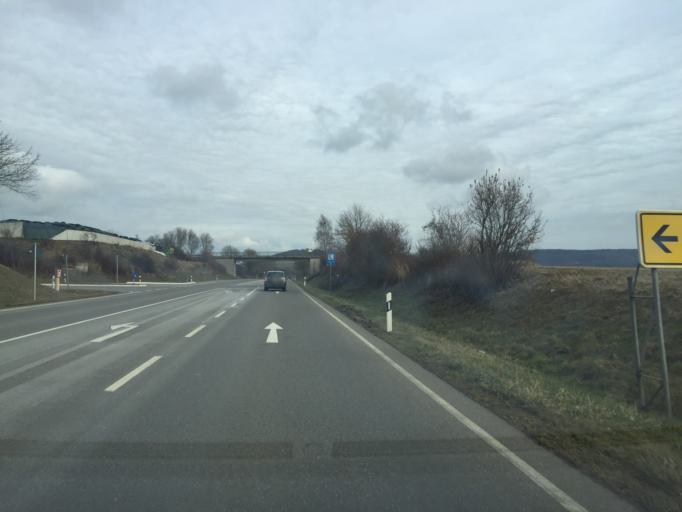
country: DE
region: Baden-Wuerttemberg
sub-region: Freiburg Region
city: Geisingen
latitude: 47.9269
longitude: 8.5758
